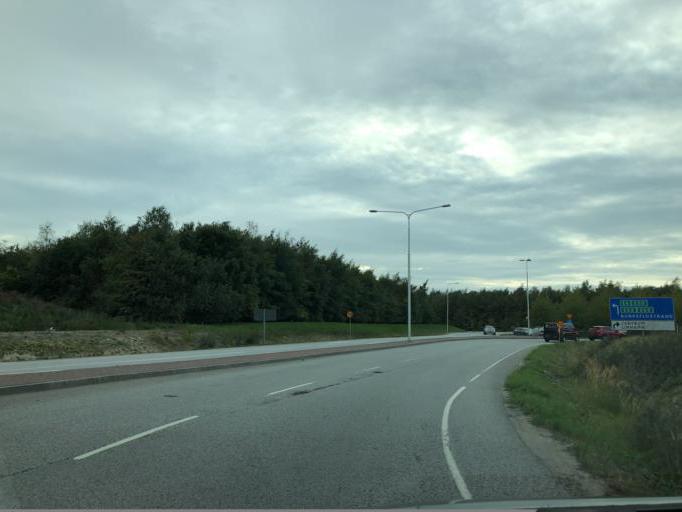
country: SE
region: Skane
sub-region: Malmo
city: Bunkeflostrand
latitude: 55.5619
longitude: 12.9655
